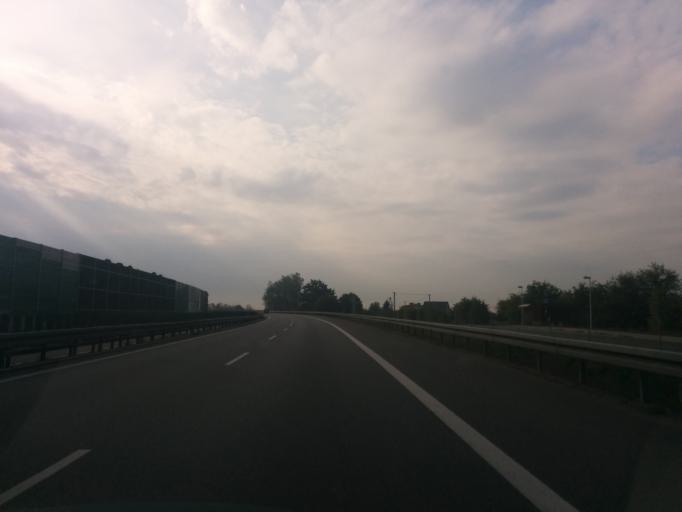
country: PL
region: Masovian Voivodeship
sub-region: Powiat bialobrzeski
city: Stara Blotnica
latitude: 51.5622
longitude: 21.0265
